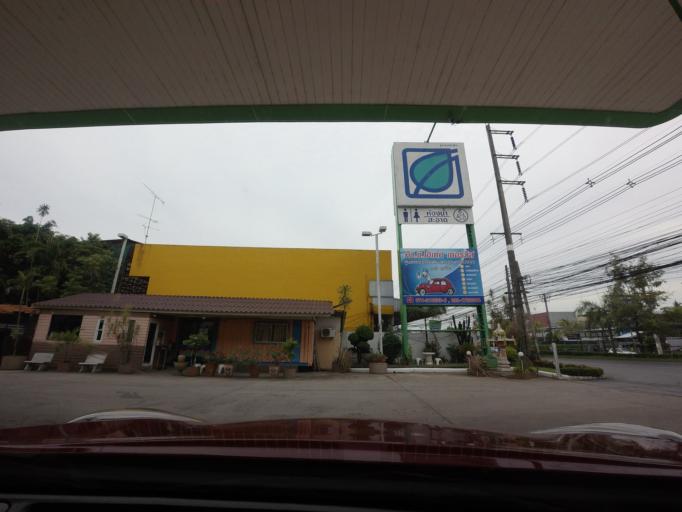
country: TH
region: Songkhla
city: Hat Yai
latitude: 6.9799
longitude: 100.4811
